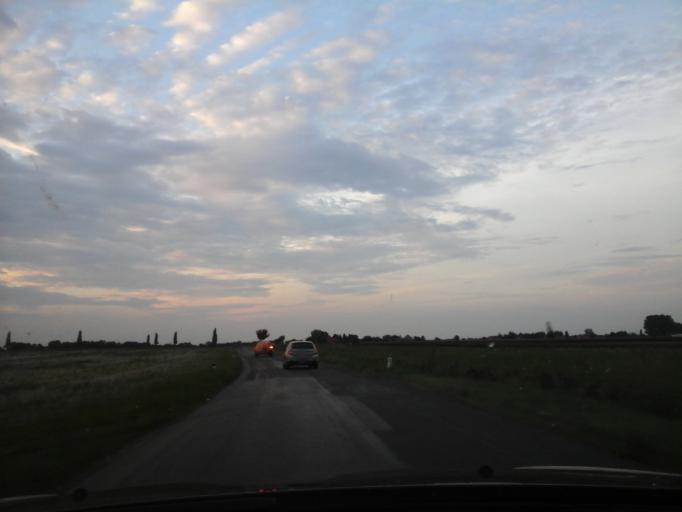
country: AT
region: Lower Austria
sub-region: Politischer Bezirk Bruck an der Leitha
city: Scharndorf
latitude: 48.1019
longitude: 16.7992
